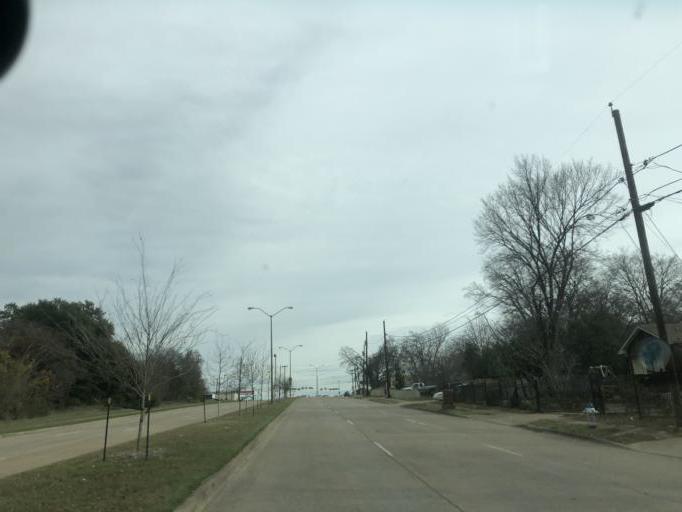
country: US
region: Texas
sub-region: Dallas County
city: Duncanville
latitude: 32.6748
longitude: -96.8257
